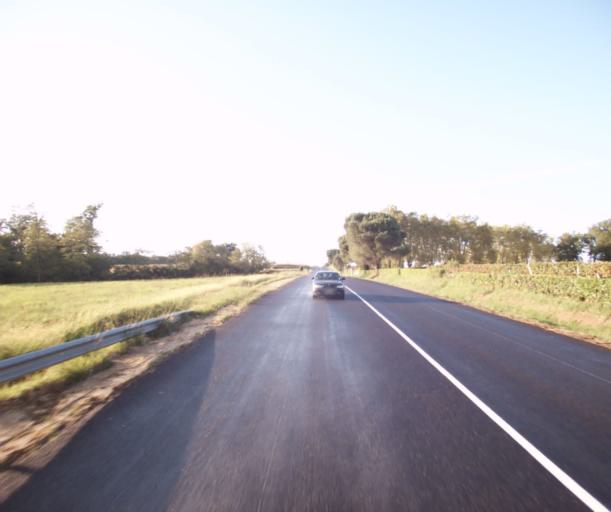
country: FR
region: Midi-Pyrenees
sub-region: Departement du Gers
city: Cazaubon
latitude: 43.9127
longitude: -0.0247
